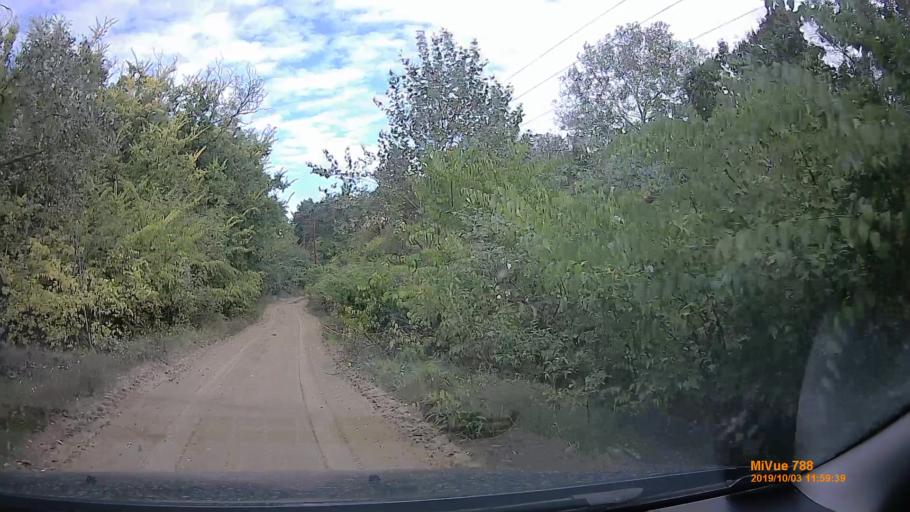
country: HU
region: Pest
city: God
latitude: 47.6714
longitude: 19.1720
